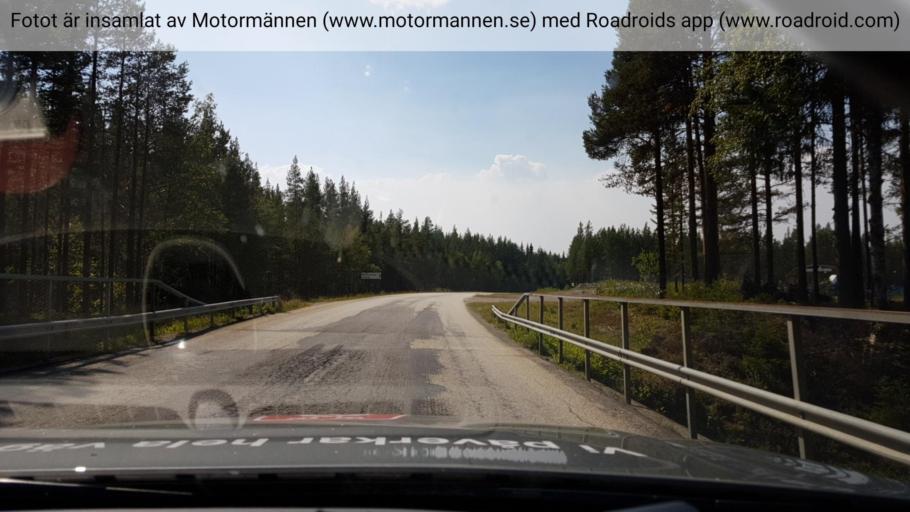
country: SE
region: Jaemtland
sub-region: Harjedalens Kommun
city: Sveg
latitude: 62.4131
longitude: 13.6156
